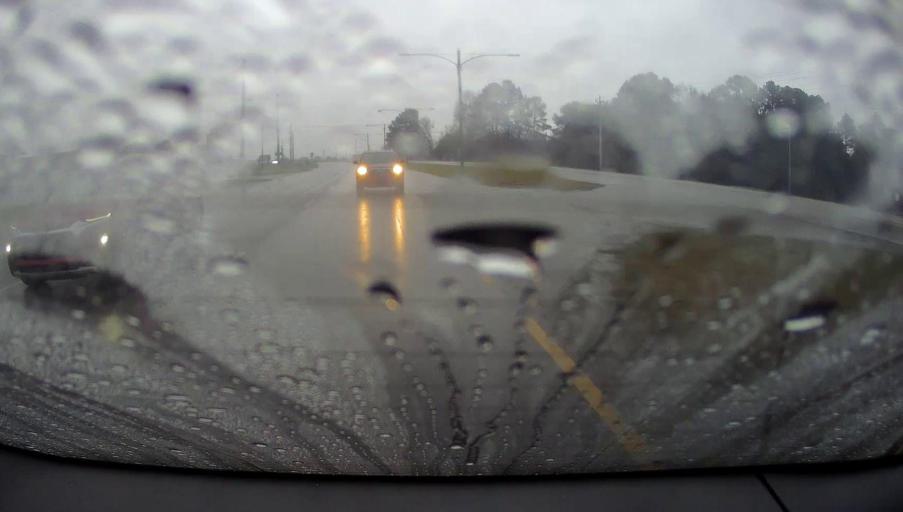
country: US
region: Alabama
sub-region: Morgan County
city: Hartselle
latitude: 34.4204
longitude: -86.9253
